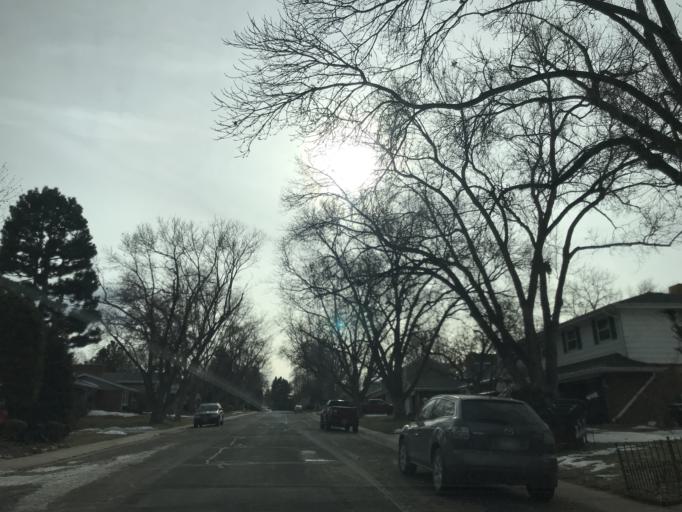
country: US
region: Colorado
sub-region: Arapahoe County
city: Littleton
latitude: 39.5926
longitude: -105.0126
